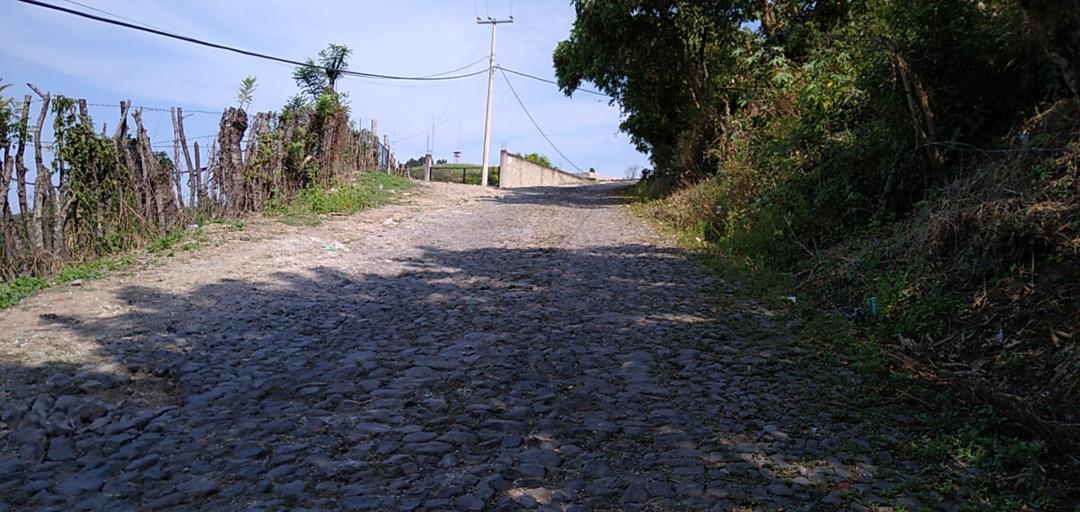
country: MX
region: Nayarit
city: Tepic
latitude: 21.5324
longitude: -104.9137
